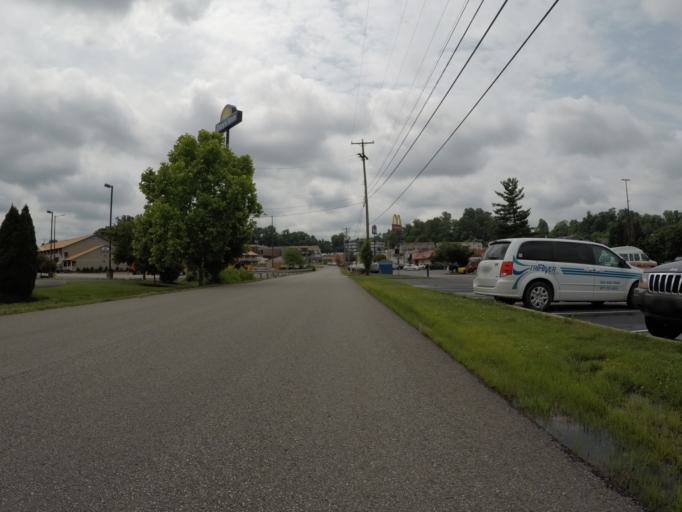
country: US
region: West Virginia
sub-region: Cabell County
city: Pea Ridge
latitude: 38.4145
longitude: -82.3439
